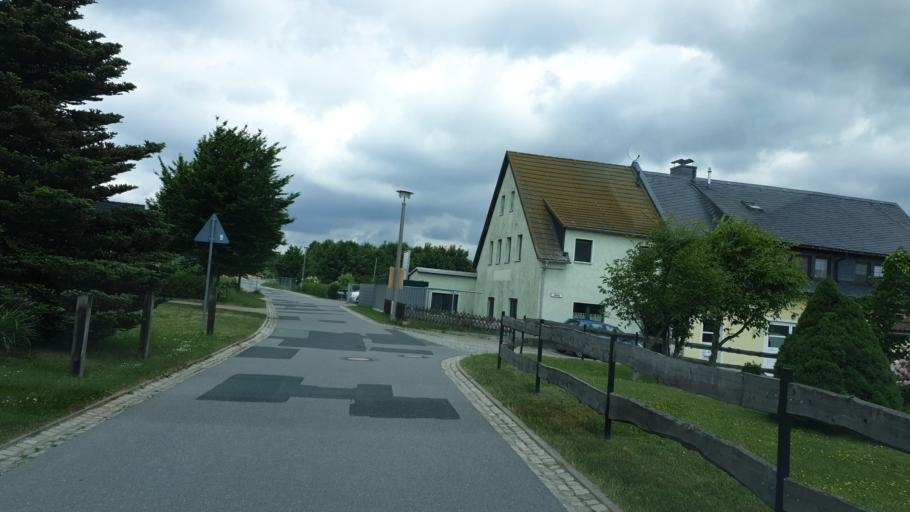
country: DE
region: Saxony
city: Marienberg
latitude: 50.6675
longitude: 13.1462
